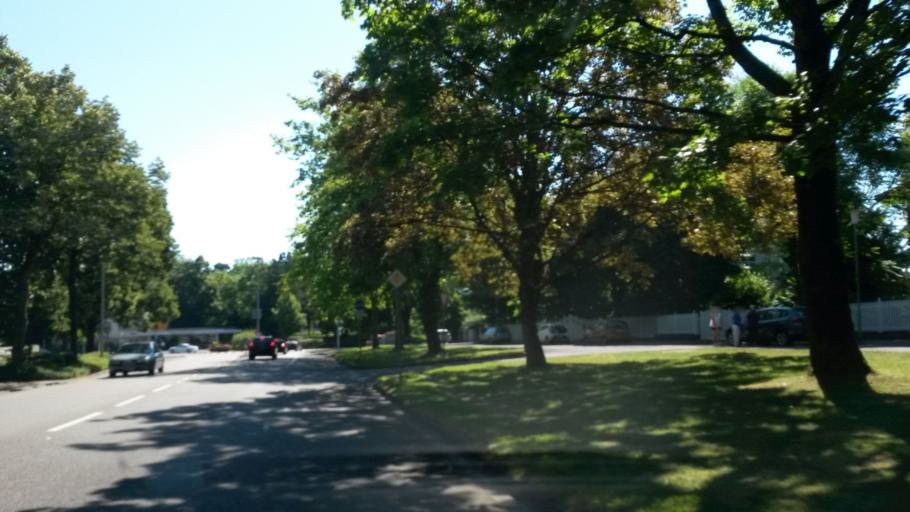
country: DE
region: Baden-Wuerttemberg
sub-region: Karlsruhe Region
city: Pforzheim
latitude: 48.8993
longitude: 8.6897
